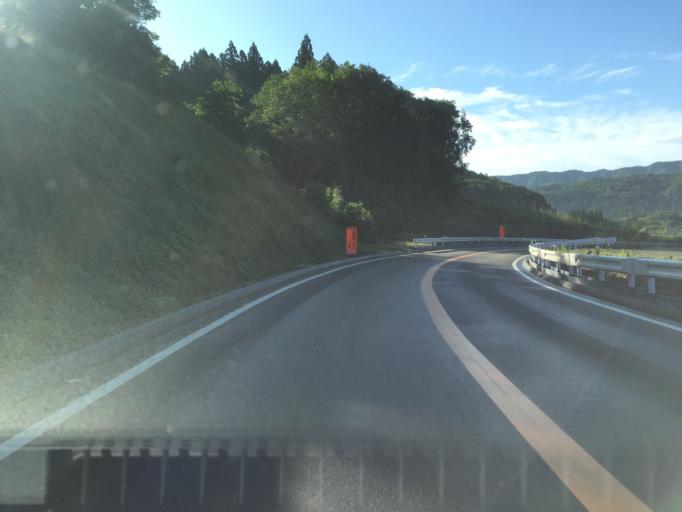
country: JP
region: Miyagi
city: Marumori
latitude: 37.7705
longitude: 140.8446
